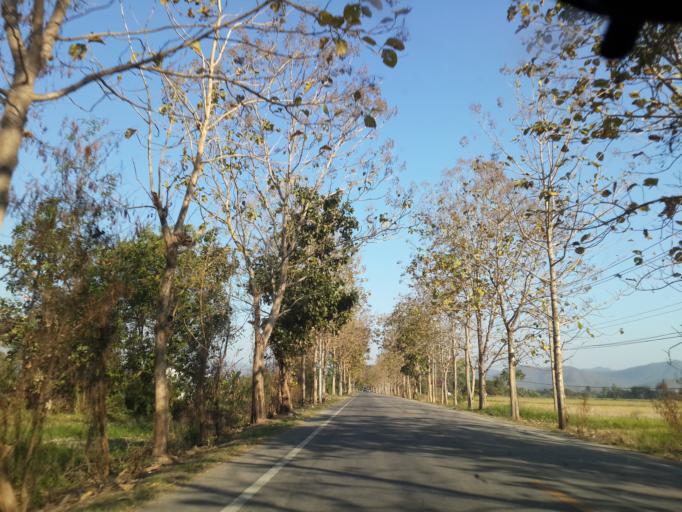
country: TH
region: Chiang Mai
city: San Kamphaeng
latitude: 18.7272
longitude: 99.1435
